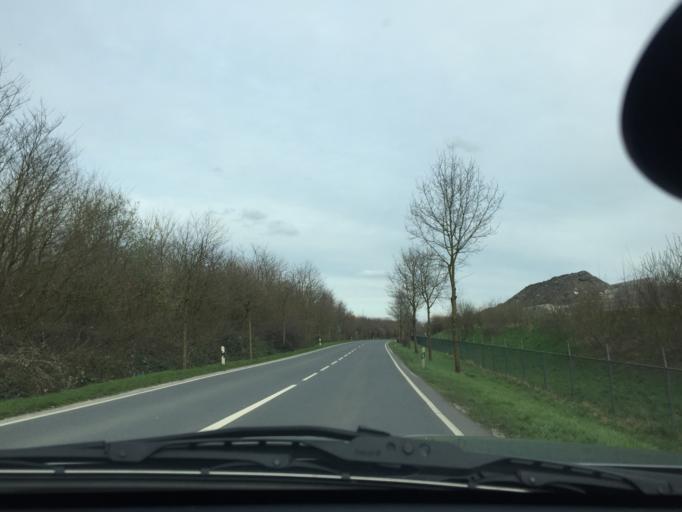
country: DE
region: North Rhine-Westphalia
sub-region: Regierungsbezirk Dusseldorf
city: Goch
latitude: 51.6977
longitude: 6.1344
